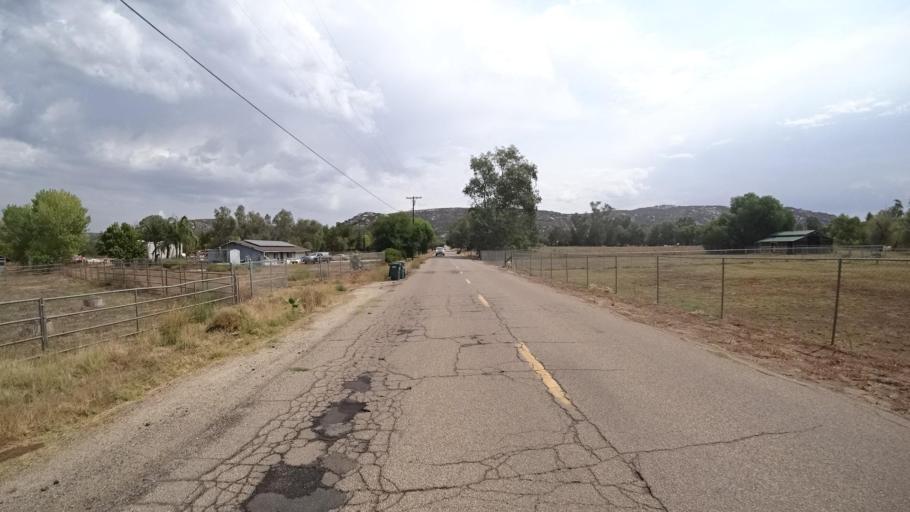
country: US
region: California
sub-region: San Diego County
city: Ramona
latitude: 33.0694
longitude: -116.8480
